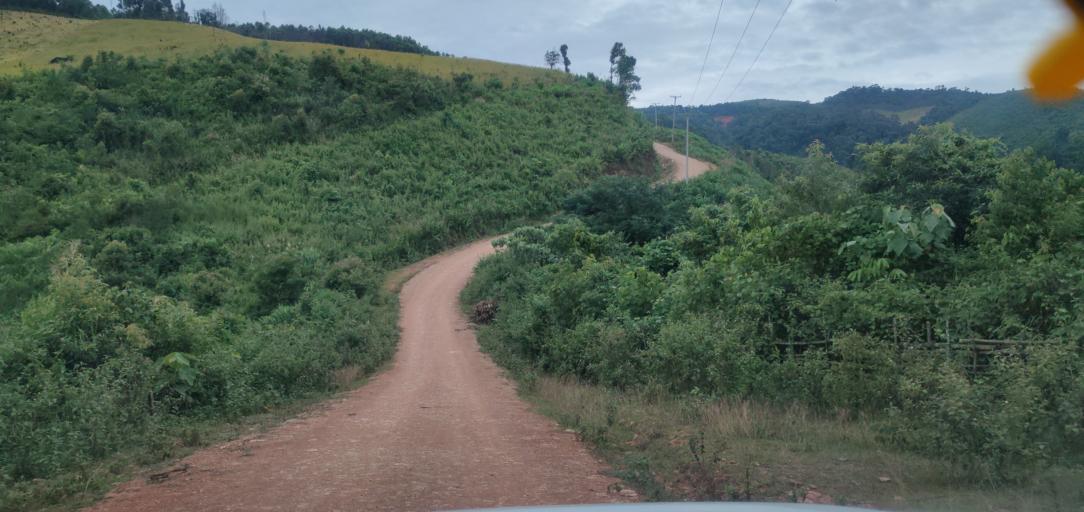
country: LA
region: Phongsali
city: Khoa
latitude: 21.1887
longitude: 102.3035
